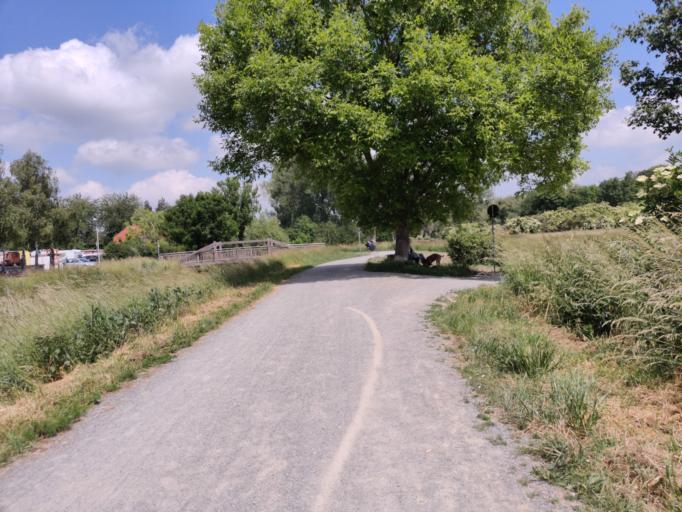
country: DE
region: Lower Saxony
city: Hildesheim
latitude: 52.1667
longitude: 9.9232
